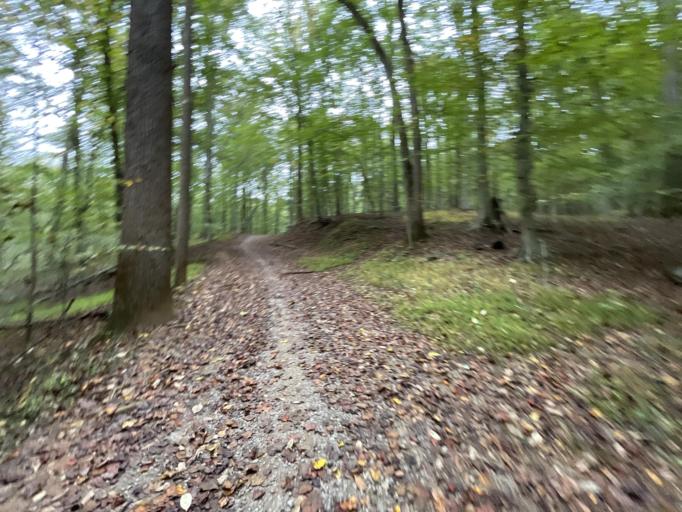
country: US
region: Maryland
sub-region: Baltimore County
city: Hampton
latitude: 39.4347
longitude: -76.5590
